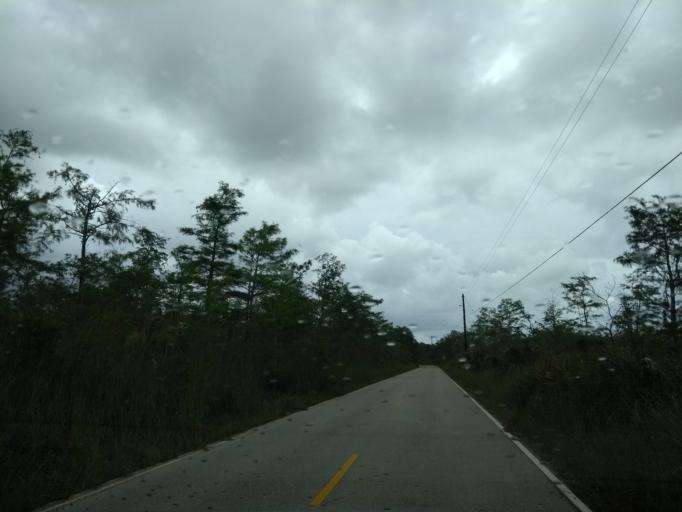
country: US
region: Florida
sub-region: Miami-Dade County
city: The Hammocks
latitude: 25.7582
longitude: -80.9293
